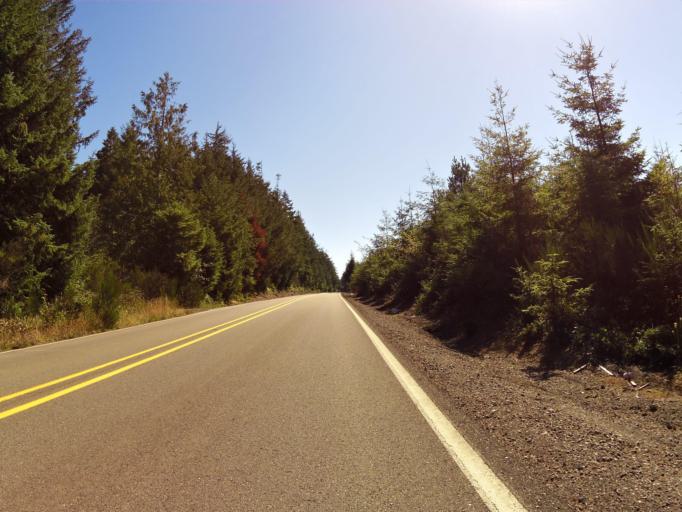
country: US
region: Oregon
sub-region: Coos County
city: Barview
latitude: 43.2385
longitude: -124.3392
